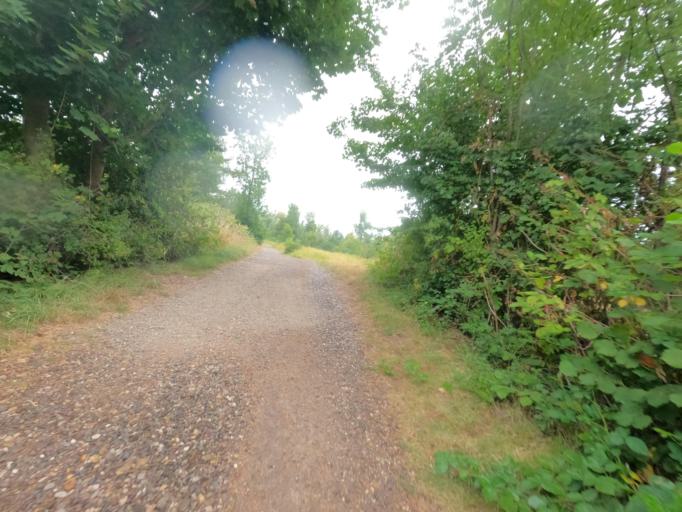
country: DE
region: North Rhine-Westphalia
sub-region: Regierungsbezirk Koln
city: Linnich
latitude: 50.9498
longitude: 6.3071
